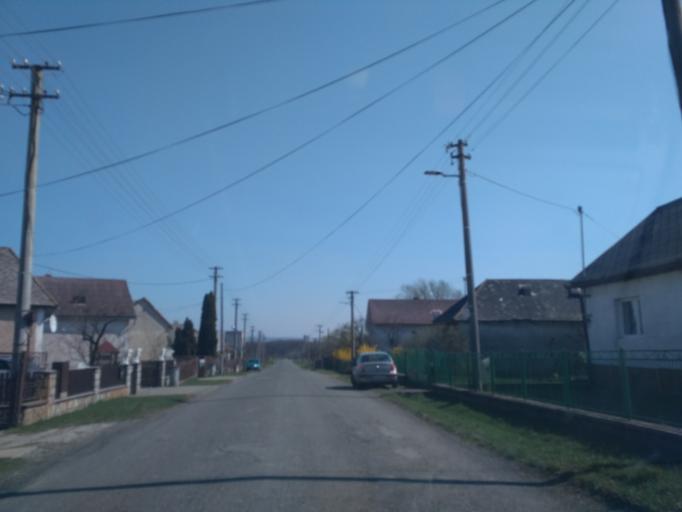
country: SK
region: Presovsky
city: Vranov nad Topl'ou
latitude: 48.8026
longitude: 21.6478
